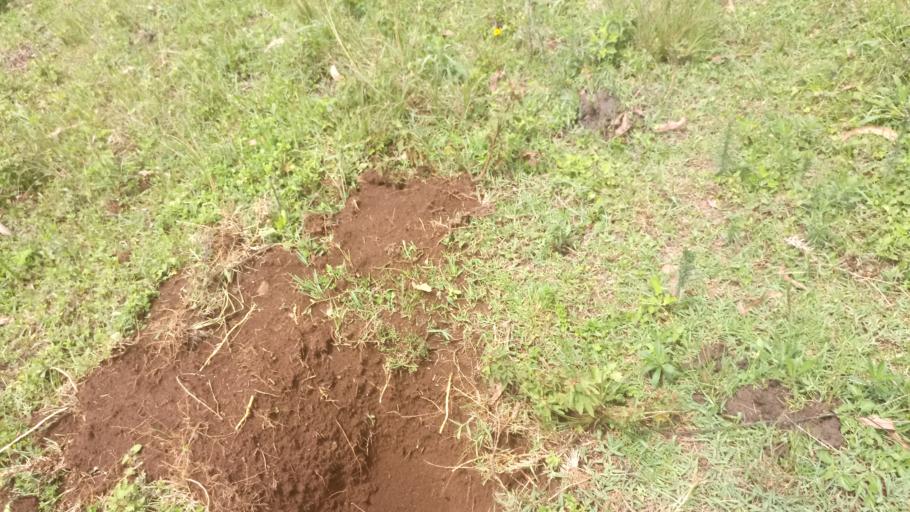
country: KE
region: Kirinyaga
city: Keruguya
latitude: -0.3990
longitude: 37.1583
